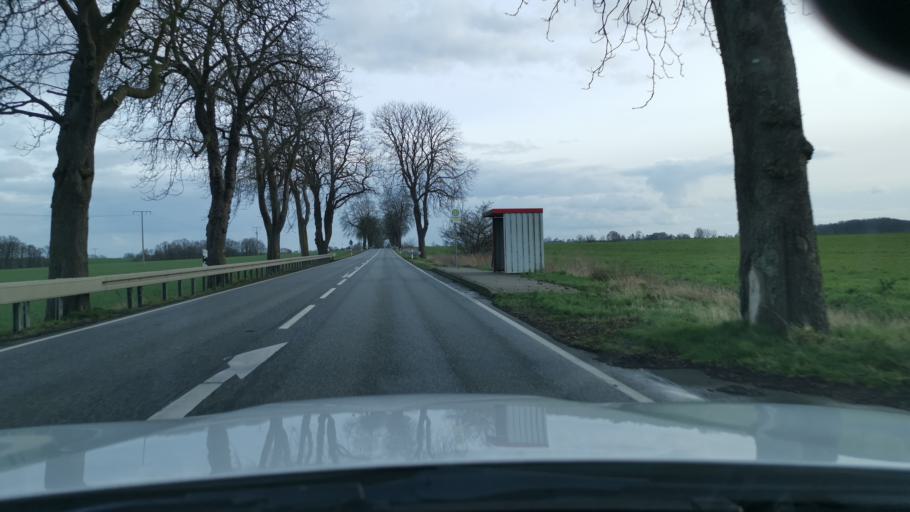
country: DE
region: Mecklenburg-Vorpommern
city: Dummerstorf
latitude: 53.9856
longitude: 12.2743
